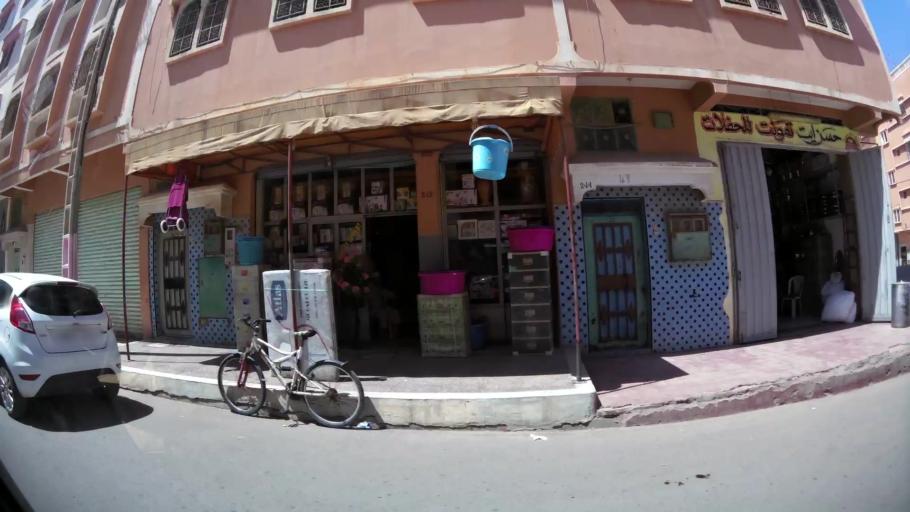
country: MA
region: Souss-Massa-Draa
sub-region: Inezgane-Ait Mellou
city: Inezgane
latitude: 30.3391
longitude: -9.5025
